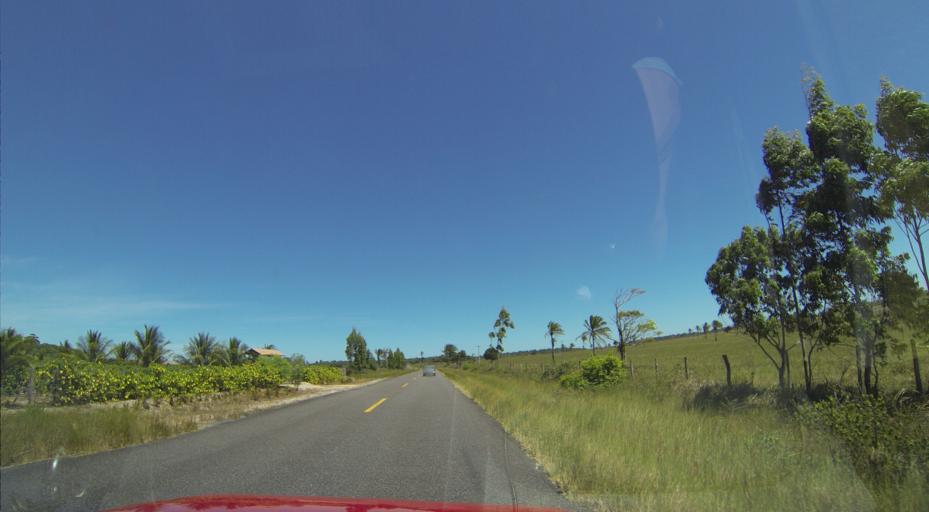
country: BR
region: Bahia
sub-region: Prado
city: Prado
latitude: -17.2640
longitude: -39.3452
